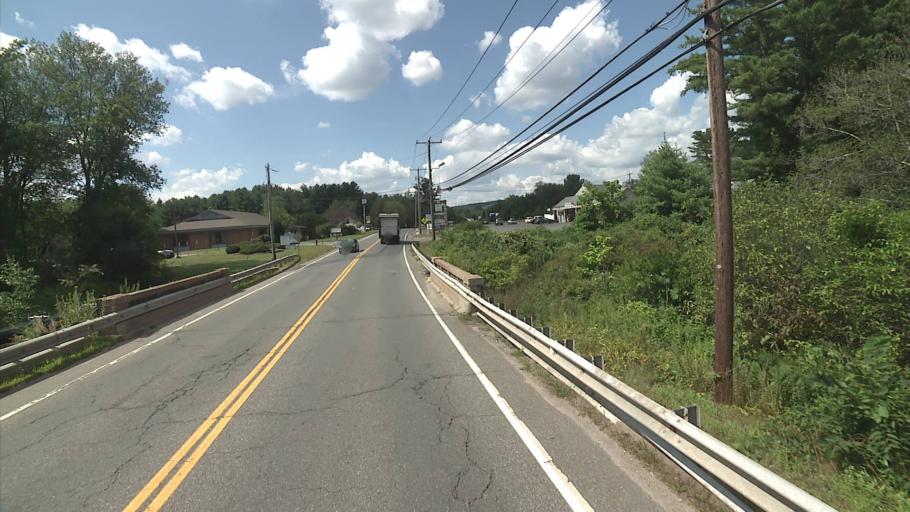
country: US
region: Connecticut
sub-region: Tolland County
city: Stafford Springs
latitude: 41.9660
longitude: -72.3285
